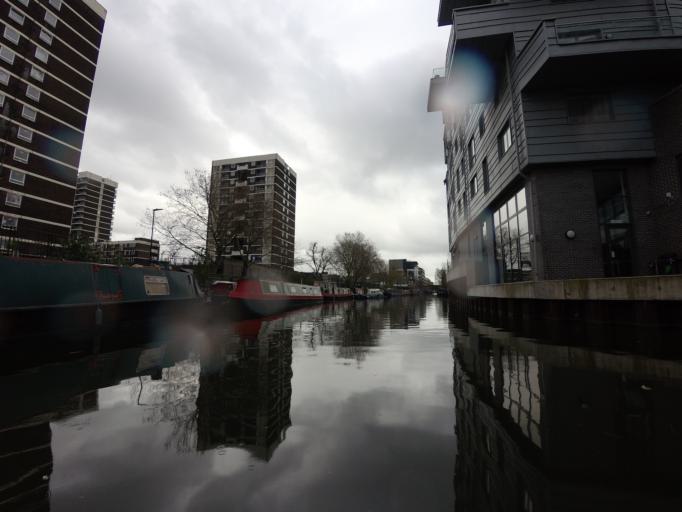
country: GB
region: England
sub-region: Greater London
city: Islington
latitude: 51.5374
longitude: -0.0846
